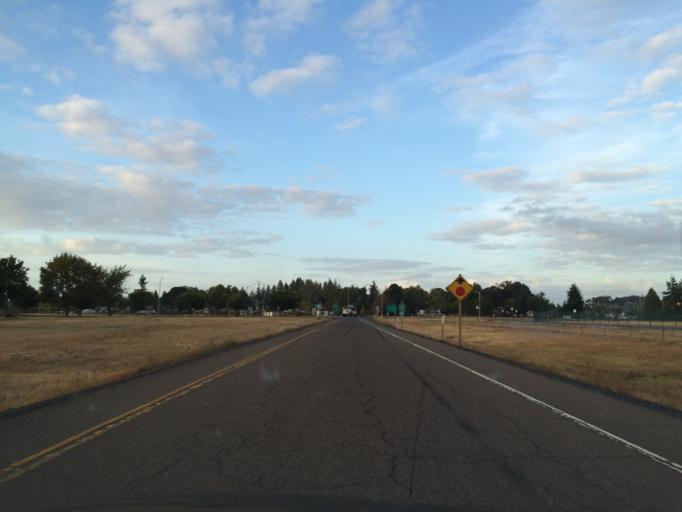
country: US
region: Oregon
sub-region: Linn County
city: Millersburg
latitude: 44.6428
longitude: -123.0609
